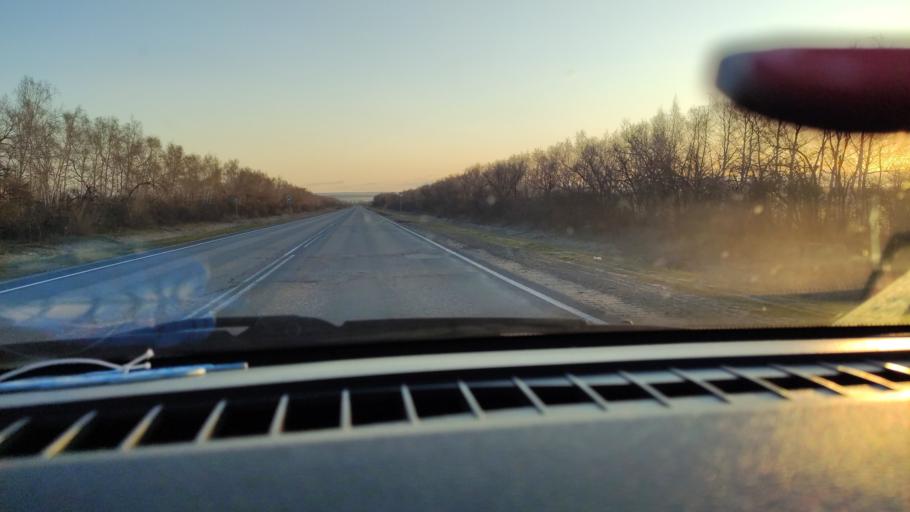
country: RU
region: Saratov
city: Sinodskoye
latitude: 51.9457
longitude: 46.6023
